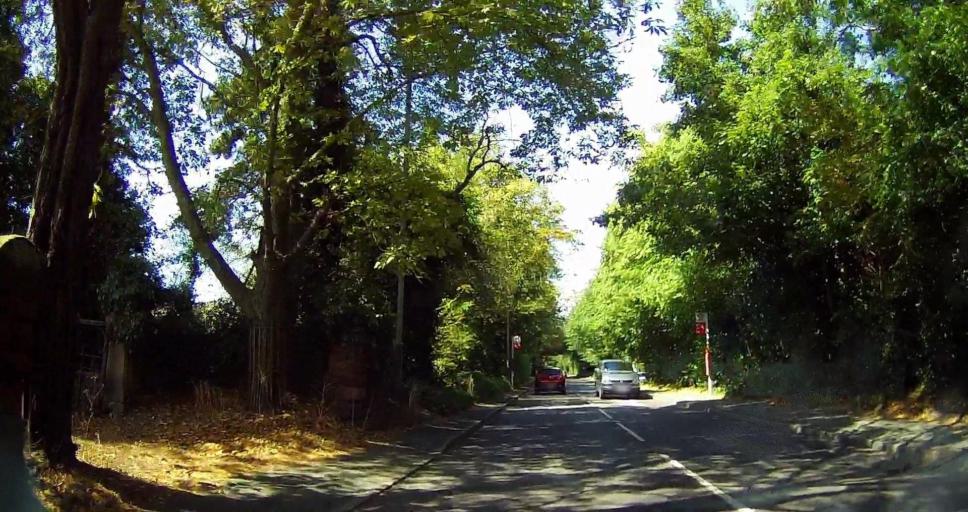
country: GB
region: England
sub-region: Staffordshire
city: Codsall
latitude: 52.6028
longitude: -2.1778
